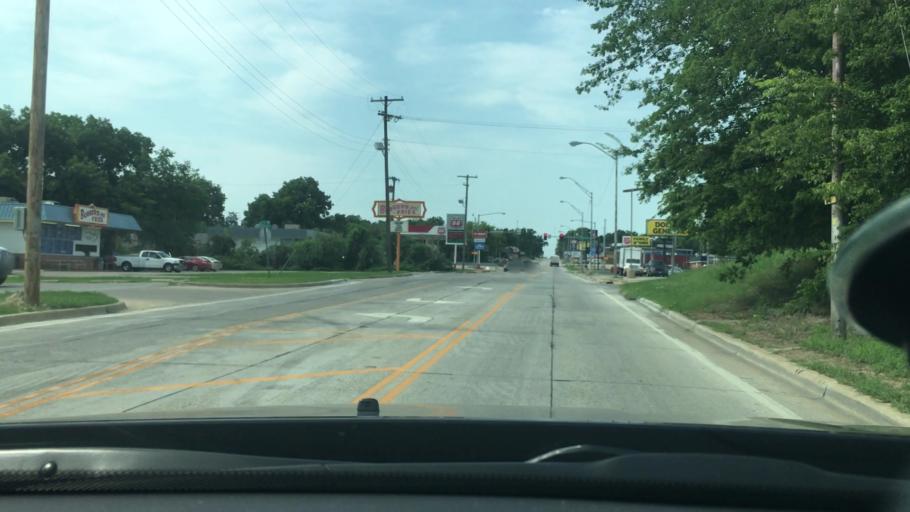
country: US
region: Oklahoma
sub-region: Carter County
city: Ardmore
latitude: 34.1861
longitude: -97.1234
